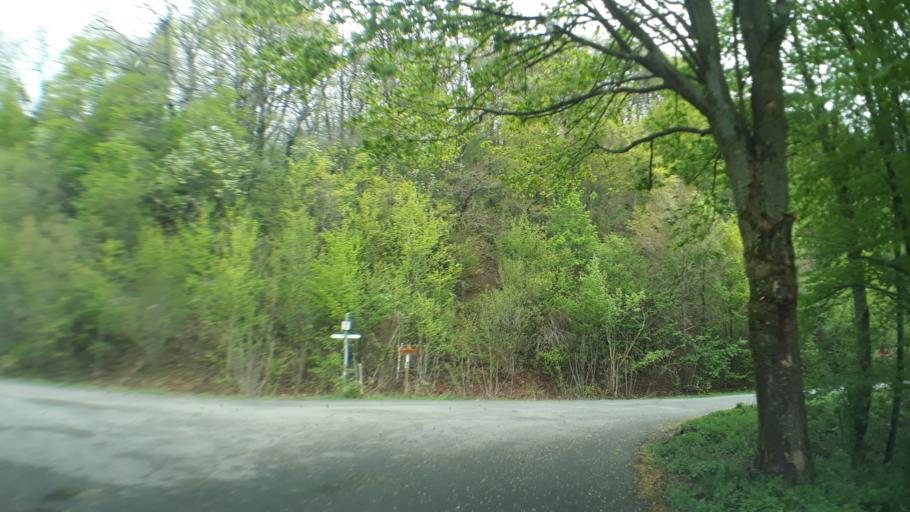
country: DE
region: North Rhine-Westphalia
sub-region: Regierungsbezirk Koln
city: Nettersheim
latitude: 50.5002
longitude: 6.6242
